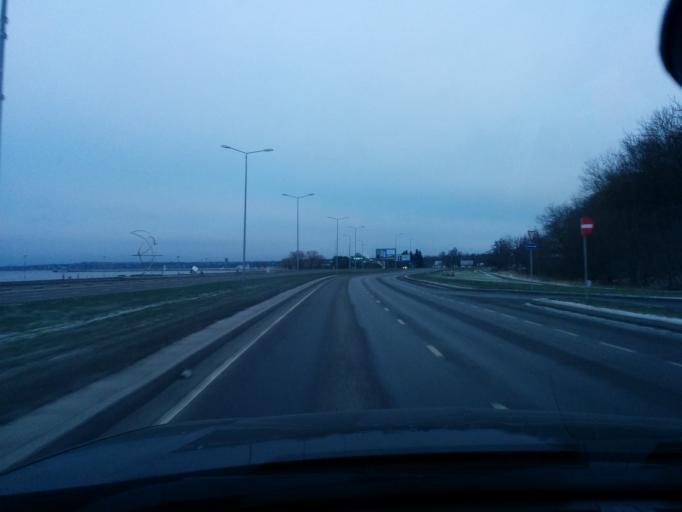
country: EE
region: Harju
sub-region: Viimsi vald
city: Viimsi
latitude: 59.4580
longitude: 24.8125
